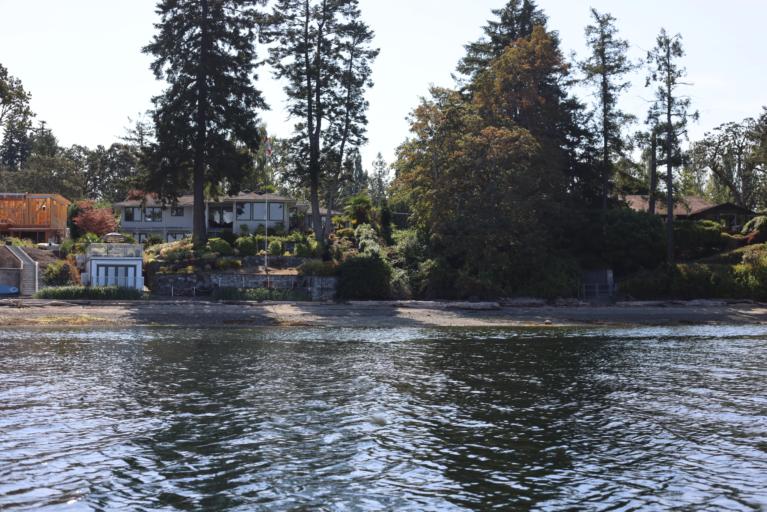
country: CA
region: British Columbia
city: North Saanich
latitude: 48.6465
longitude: -123.4633
